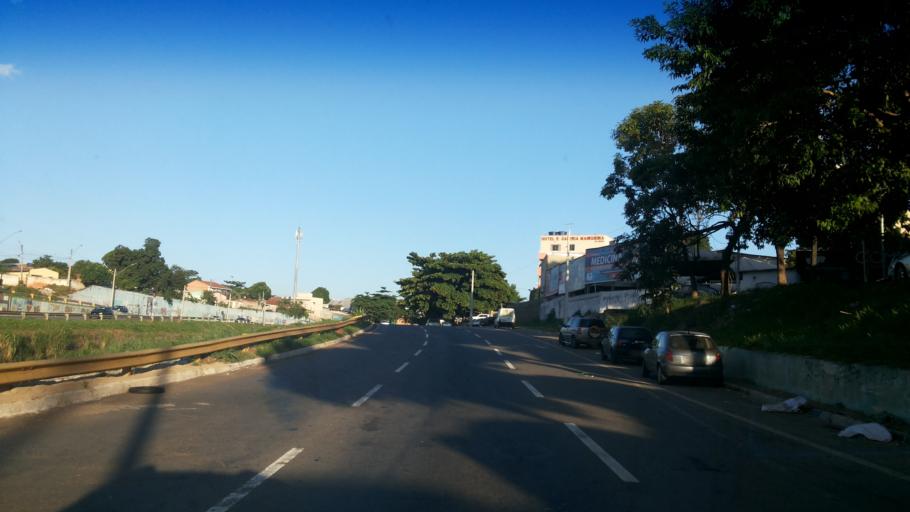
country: BR
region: Goias
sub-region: Goiania
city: Goiania
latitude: -16.6580
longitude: -49.2552
